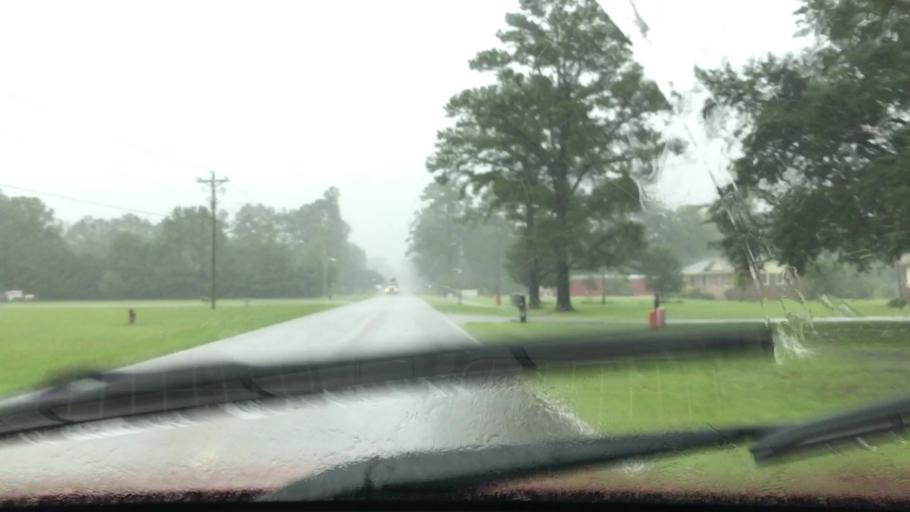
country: US
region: South Carolina
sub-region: Horry County
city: Red Hill
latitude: 33.8811
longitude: -78.9672
